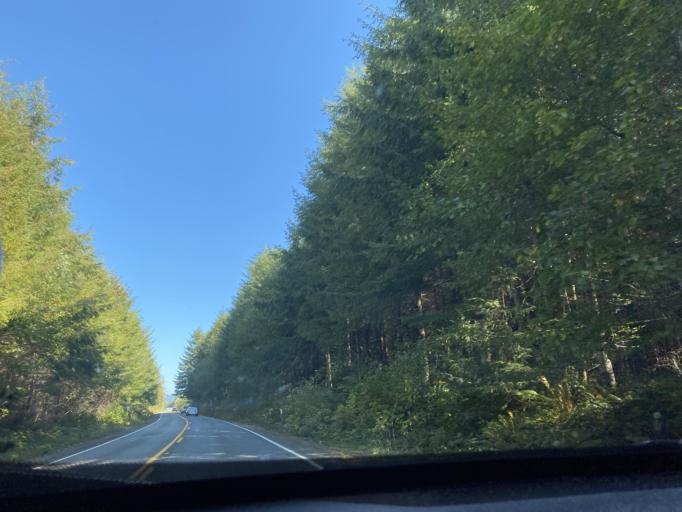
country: US
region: Washington
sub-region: Clallam County
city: Forks
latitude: 47.9229
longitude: -124.5004
